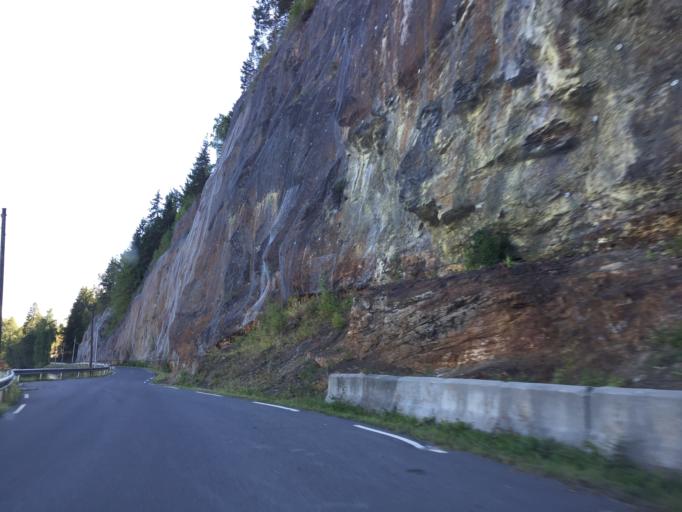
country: NO
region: Buskerud
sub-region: Ovre Eiker
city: Hokksund
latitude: 59.6800
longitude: 9.8609
